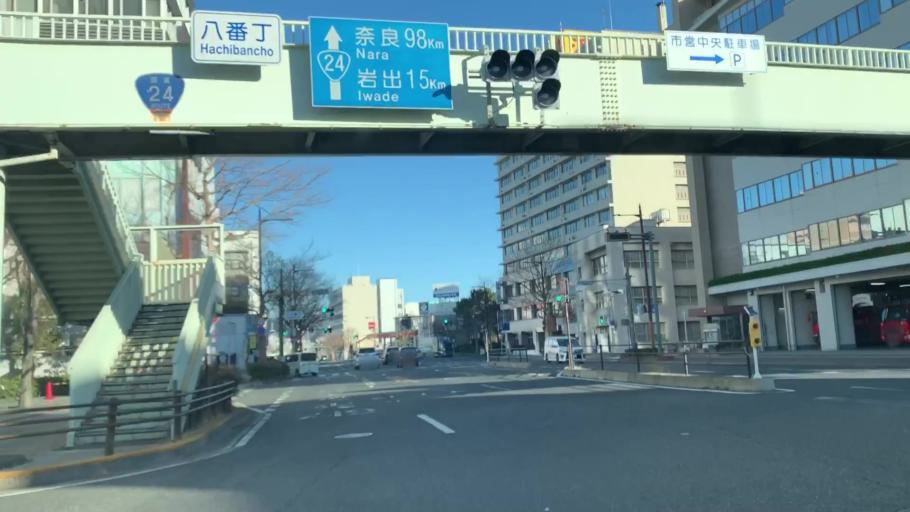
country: JP
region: Wakayama
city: Wakayama-shi
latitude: 34.2309
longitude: 135.1693
